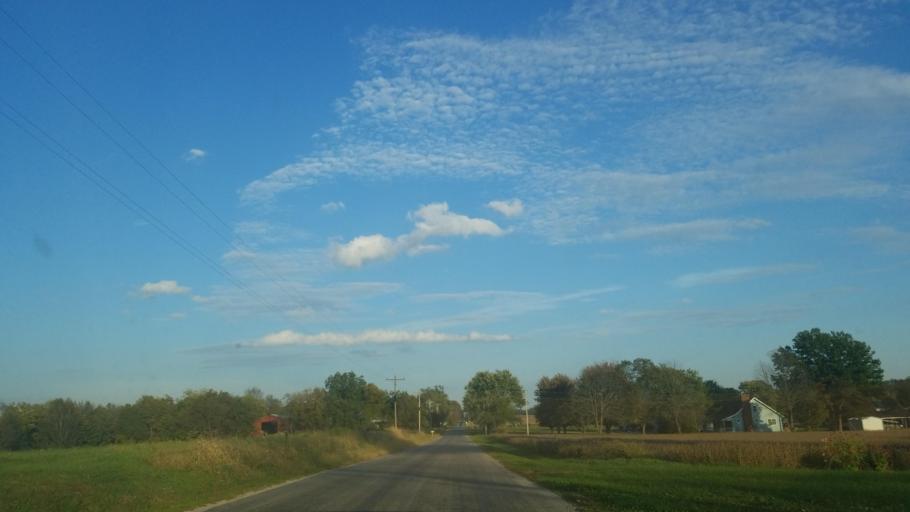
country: US
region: Illinois
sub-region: Saline County
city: Carrier Mills
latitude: 37.8050
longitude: -88.6555
